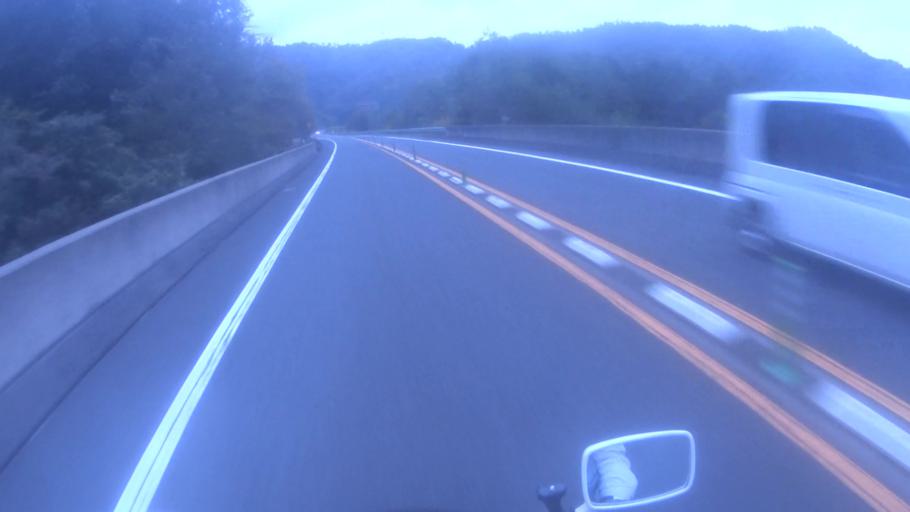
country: JP
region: Kyoto
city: Ayabe
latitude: 35.3753
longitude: 135.2670
